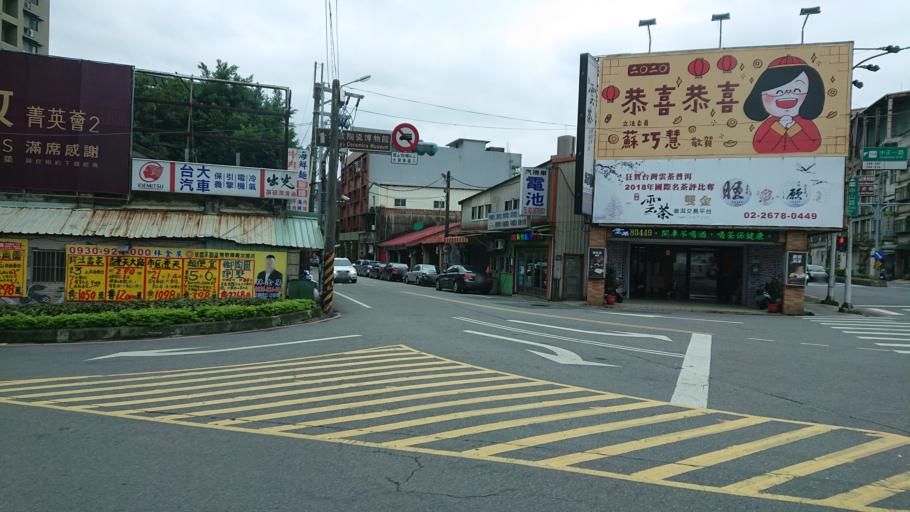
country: TW
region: Taiwan
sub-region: Taoyuan
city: Taoyuan
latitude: 24.9569
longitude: 121.3534
